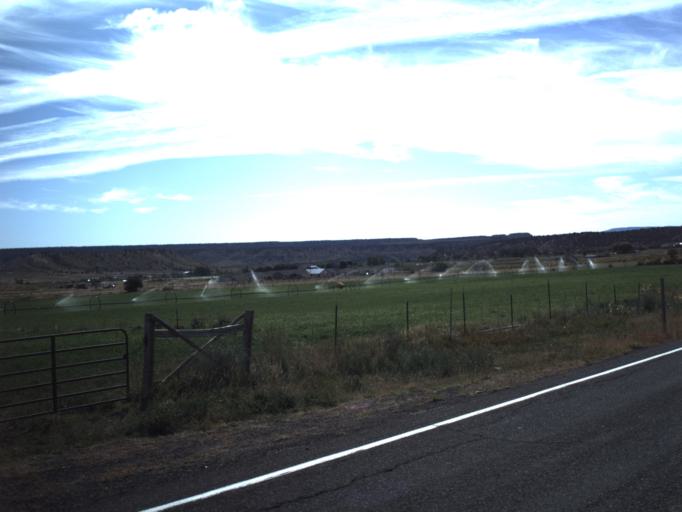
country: US
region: Utah
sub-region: Garfield County
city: Panguitch
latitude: 37.6348
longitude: -112.0819
